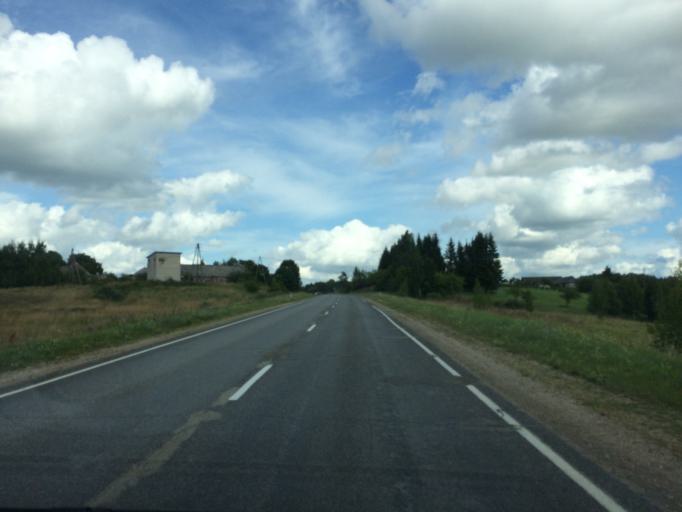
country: LV
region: Rezekne
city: Rezekne
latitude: 56.6115
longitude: 27.4436
